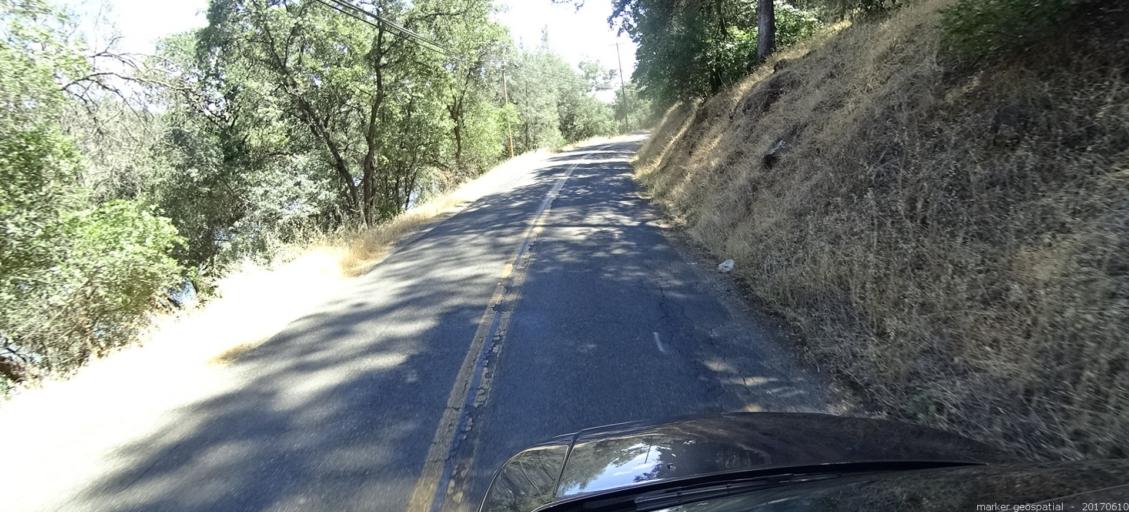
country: US
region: California
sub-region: Butte County
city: Oroville
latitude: 39.5395
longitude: -121.5463
